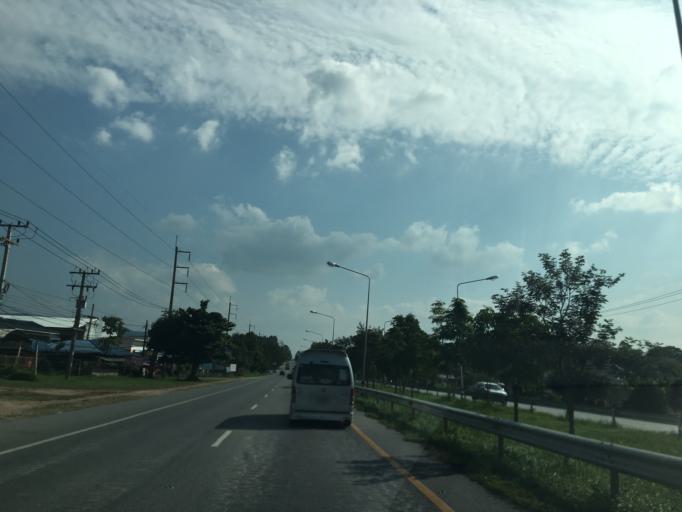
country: TH
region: Chiang Rai
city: Mae Lao
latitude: 19.7027
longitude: 99.7193
